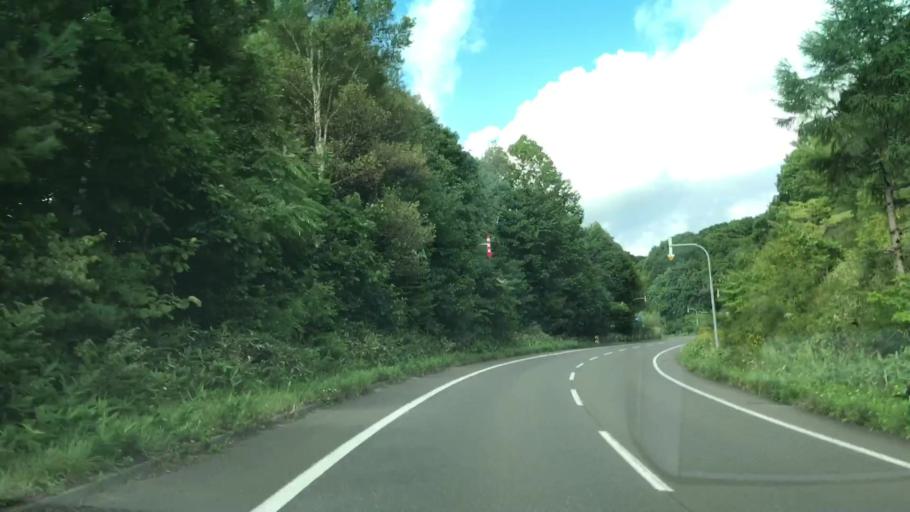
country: JP
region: Hokkaido
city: Muroran
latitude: 42.3711
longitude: 140.9589
